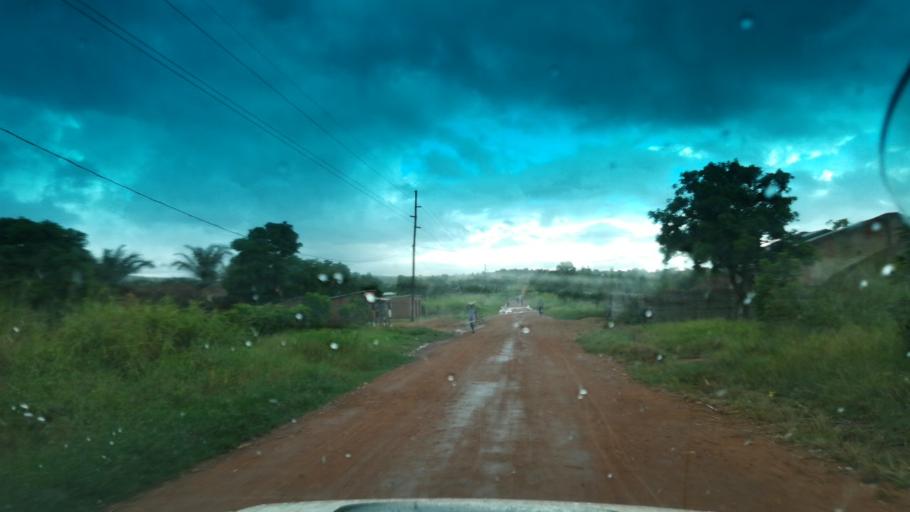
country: ZM
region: Northern
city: Kaputa
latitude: -8.4571
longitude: 28.9043
